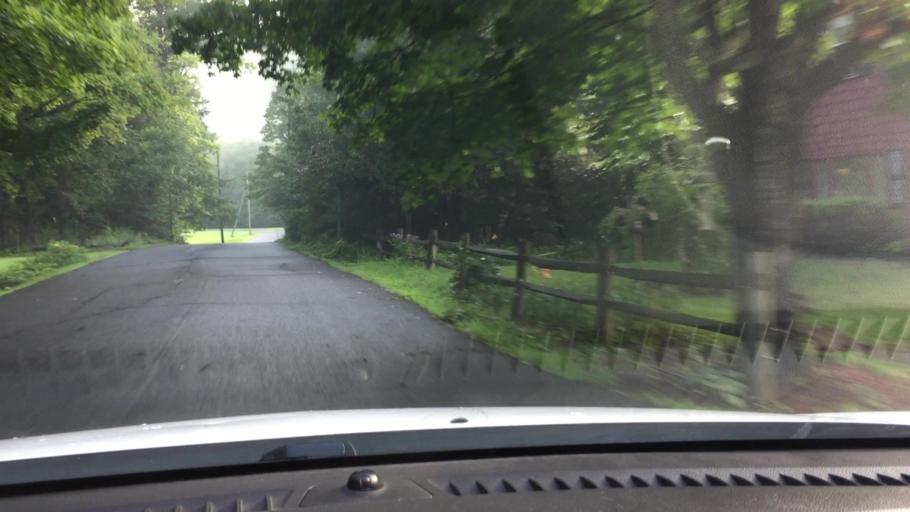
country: US
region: Massachusetts
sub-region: Berkshire County
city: Becket
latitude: 42.3688
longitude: -72.9665
